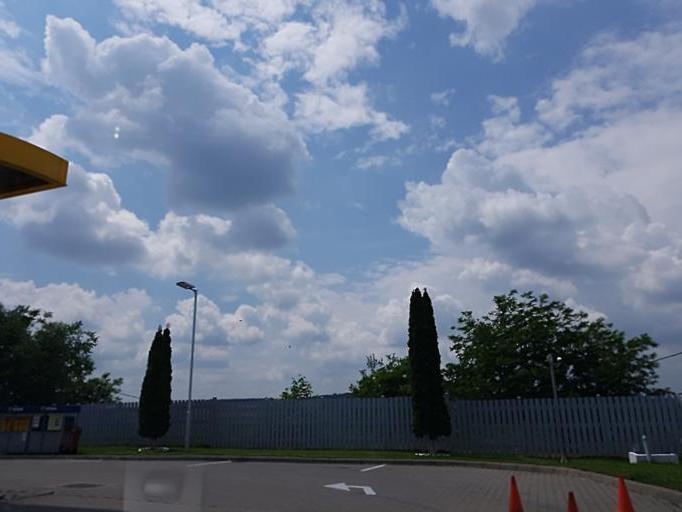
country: RO
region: Alba
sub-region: Municipiul Blaj
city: Veza
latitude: 46.1691
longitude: 23.9449
